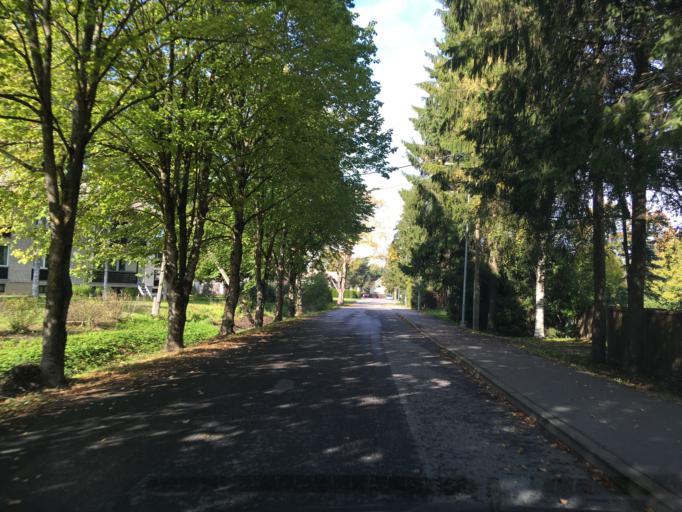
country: EE
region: Harju
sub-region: Saue vald
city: Laagri
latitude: 59.3509
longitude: 24.6375
